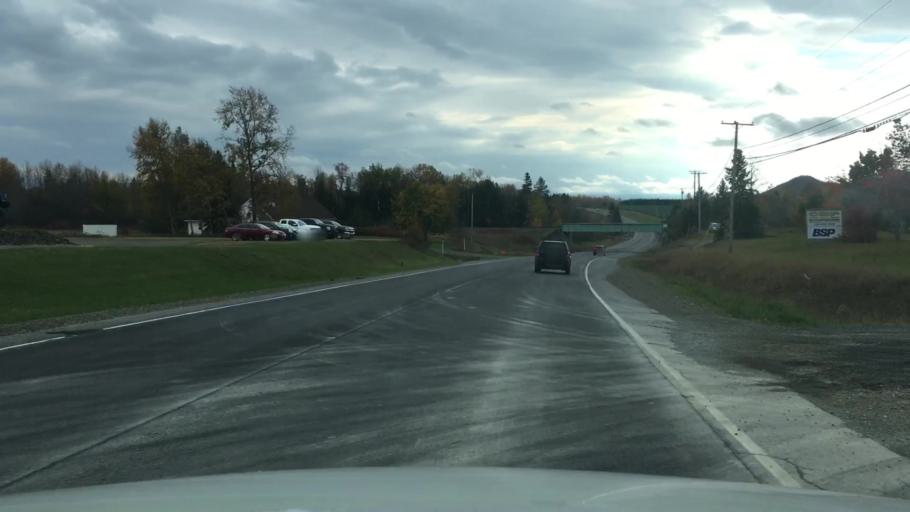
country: US
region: Maine
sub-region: Aroostook County
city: Presque Isle
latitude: 46.6524
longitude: -68.0042
